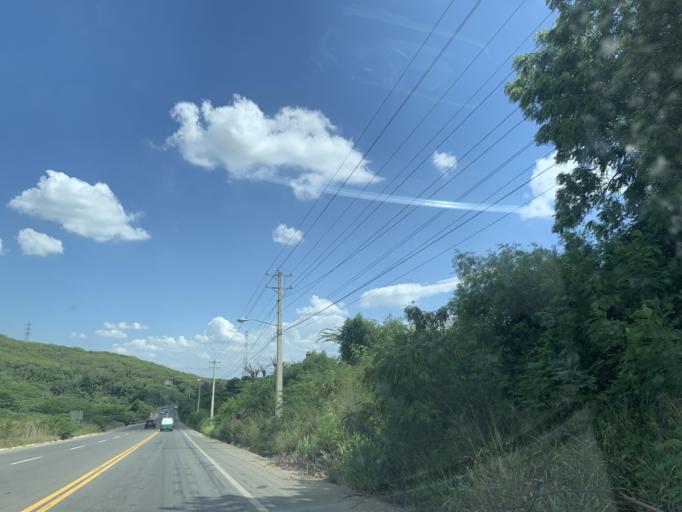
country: DO
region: Santiago
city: Villa Bisono
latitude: 19.5843
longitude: -70.8459
